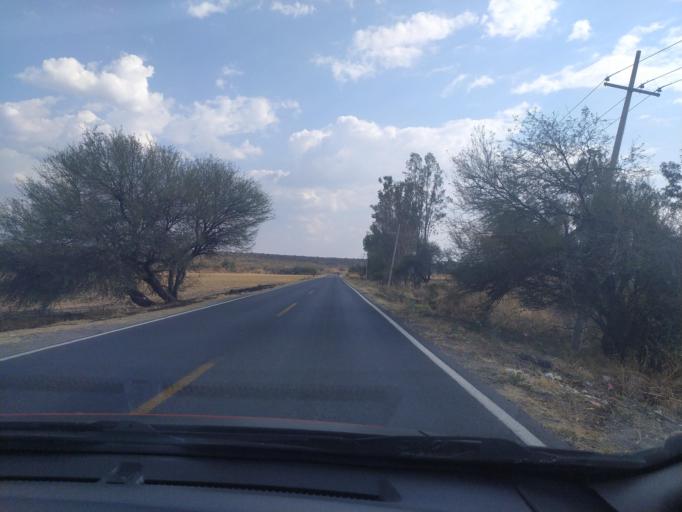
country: MX
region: Guanajuato
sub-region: San Francisco del Rincon
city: San Ignacio de Hidalgo
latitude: 20.9320
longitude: -101.8527
